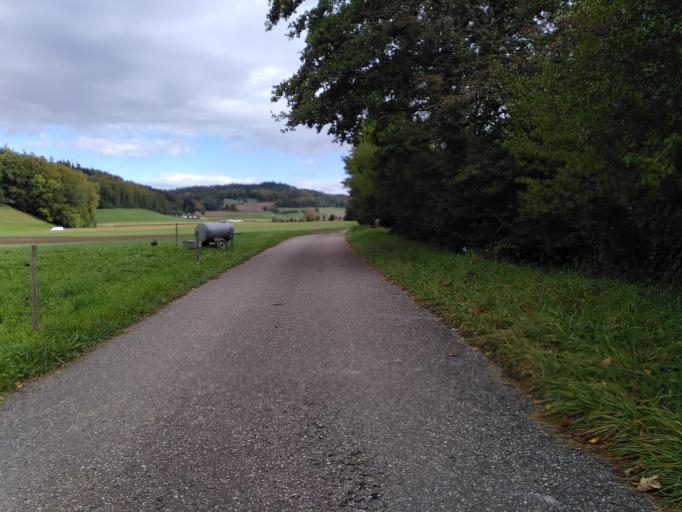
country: CH
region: Bern
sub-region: Emmental District
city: Wynigen
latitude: 47.1196
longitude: 7.6703
